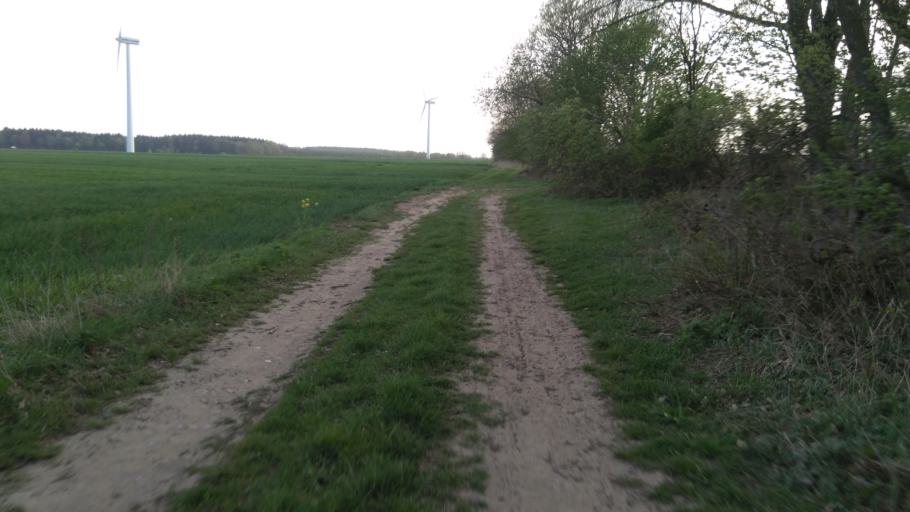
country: DE
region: Lower Saxony
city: Nottensdorf
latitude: 53.4552
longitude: 9.5988
